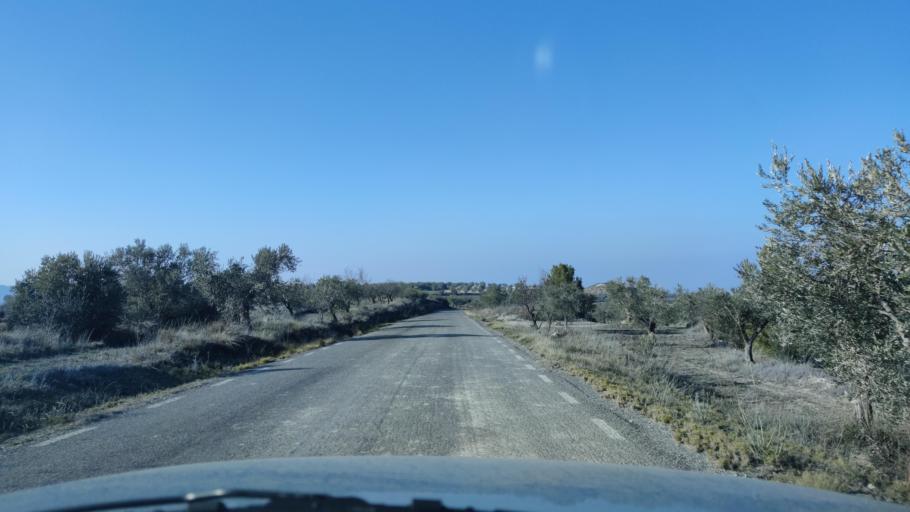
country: ES
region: Catalonia
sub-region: Provincia de Lleida
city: Torrebesses
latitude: 41.4388
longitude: 0.5620
